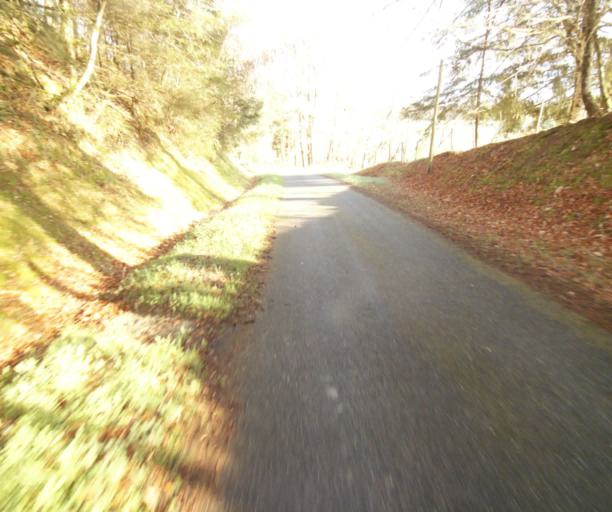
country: FR
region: Limousin
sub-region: Departement de la Correze
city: Correze
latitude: 45.2941
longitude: 1.8560
